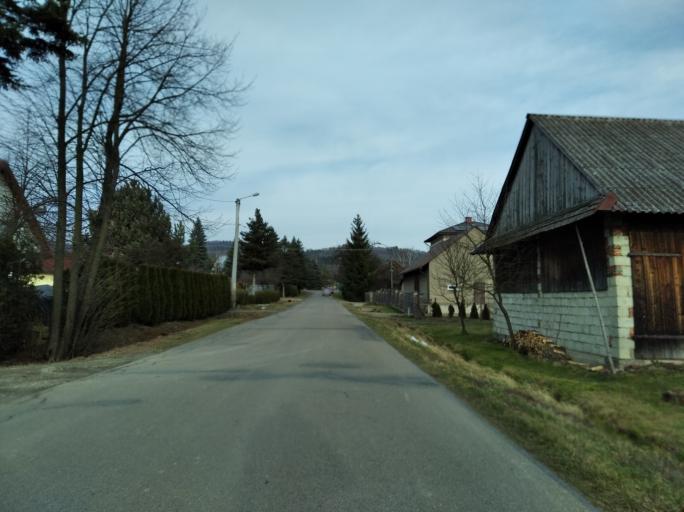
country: PL
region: Subcarpathian Voivodeship
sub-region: Powiat brzozowski
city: Blizne
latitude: 49.7520
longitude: 21.9724
